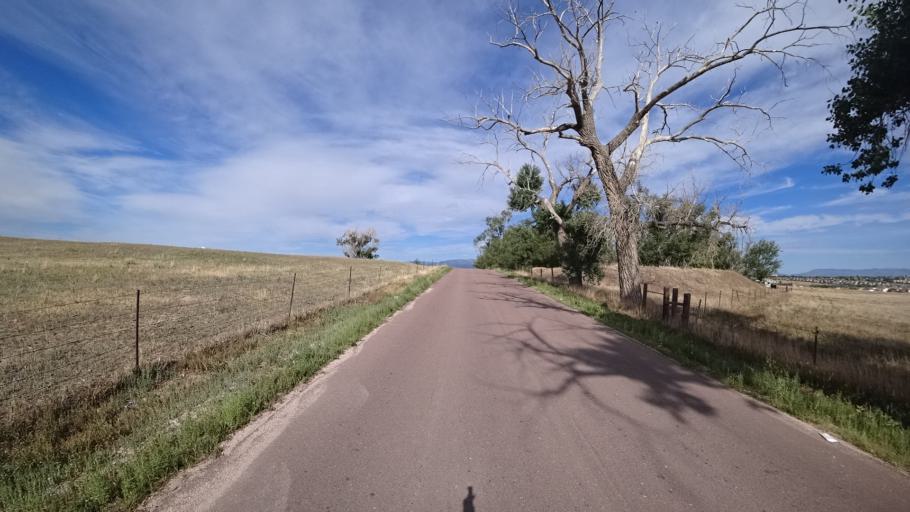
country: US
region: Colorado
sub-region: El Paso County
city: Fountain
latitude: 38.6864
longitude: -104.6748
